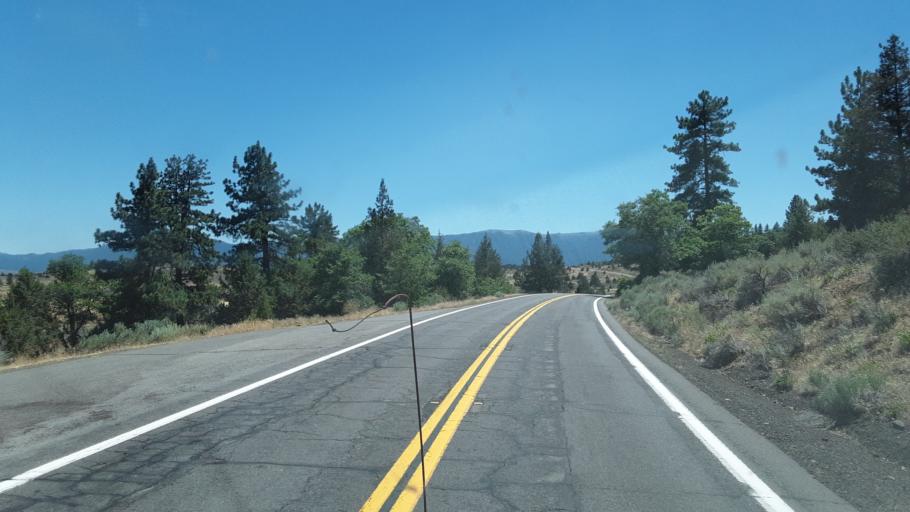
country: US
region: California
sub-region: Lassen County
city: Susanville
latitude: 40.4609
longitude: -120.6178
